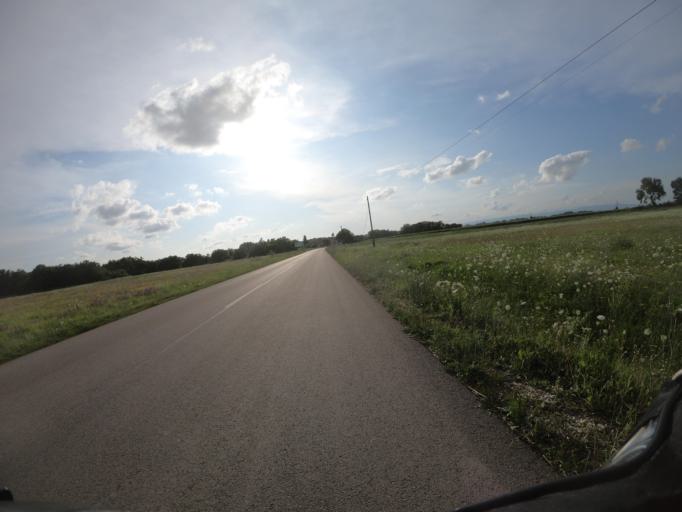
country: HU
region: Borsod-Abauj-Zemplen
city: Mezokeresztes
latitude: 47.8308
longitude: 20.7895
